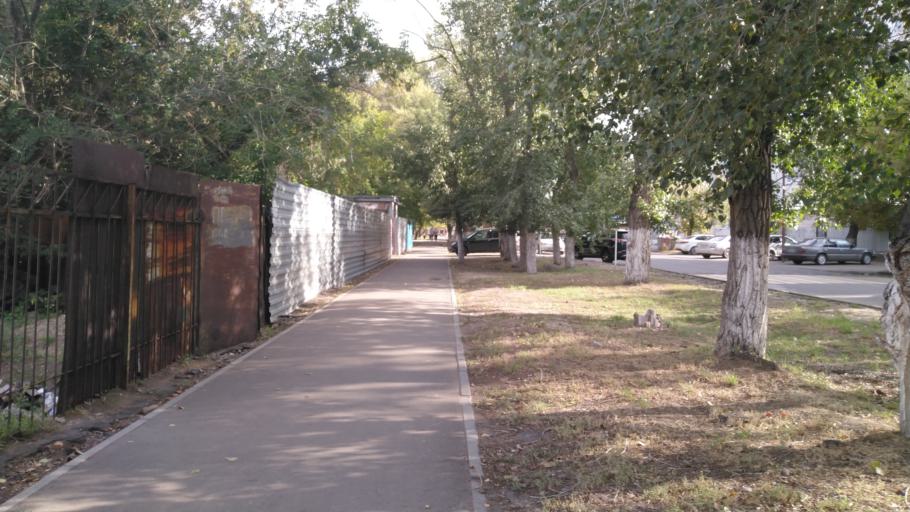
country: KZ
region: Pavlodar
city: Pavlodar
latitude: 52.2765
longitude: 76.9466
